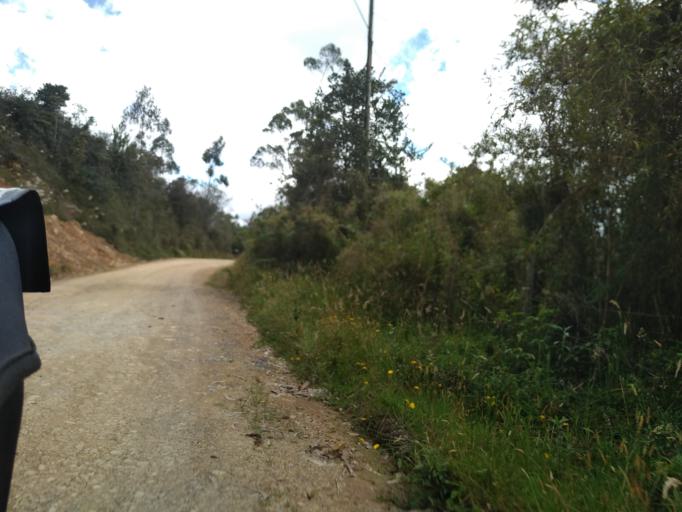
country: CO
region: Boyaca
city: Duitama
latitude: 5.9413
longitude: -73.1272
